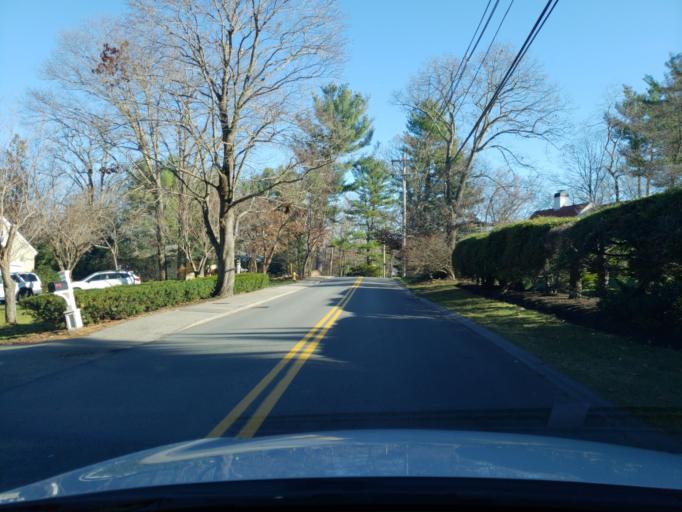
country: US
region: Massachusetts
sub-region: Essex County
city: Andover
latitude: 42.6581
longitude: -71.1215
